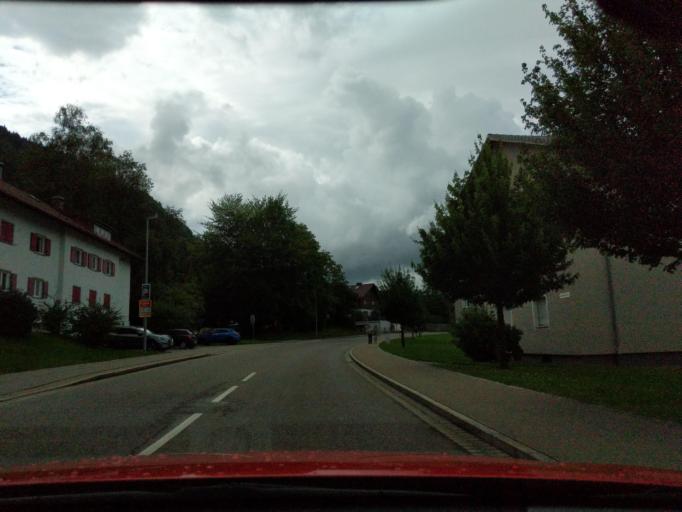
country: DE
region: Bavaria
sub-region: Swabia
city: Immenstadt im Allgau
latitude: 47.5608
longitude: 10.2065
